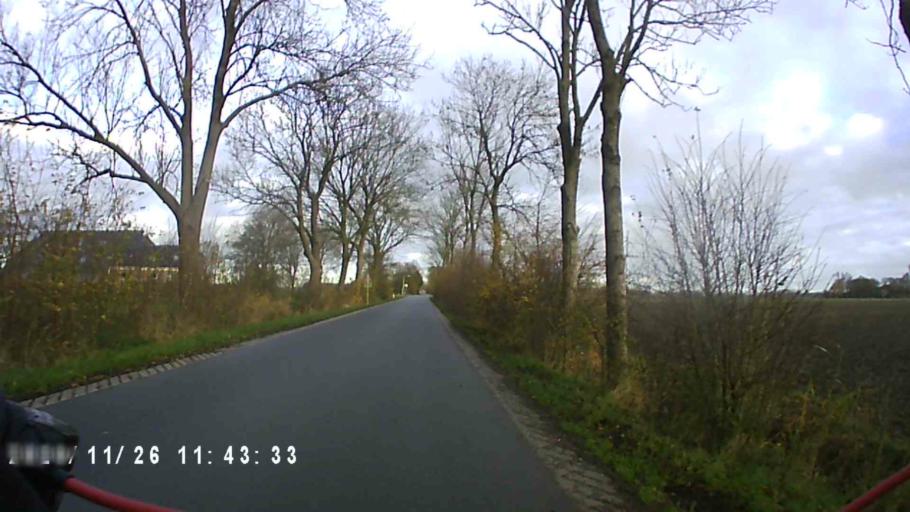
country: NL
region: Groningen
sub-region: Gemeente Bedum
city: Bedum
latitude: 53.2987
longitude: 6.5748
